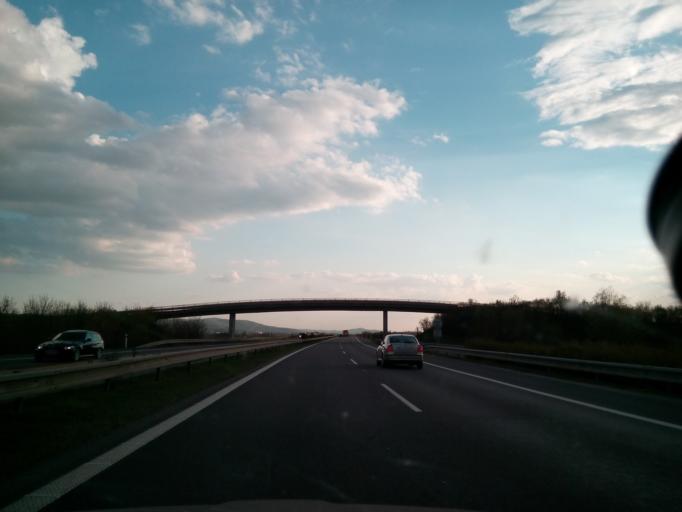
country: SK
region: Nitriansky
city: Ilava
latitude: 49.0297
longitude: 18.2677
